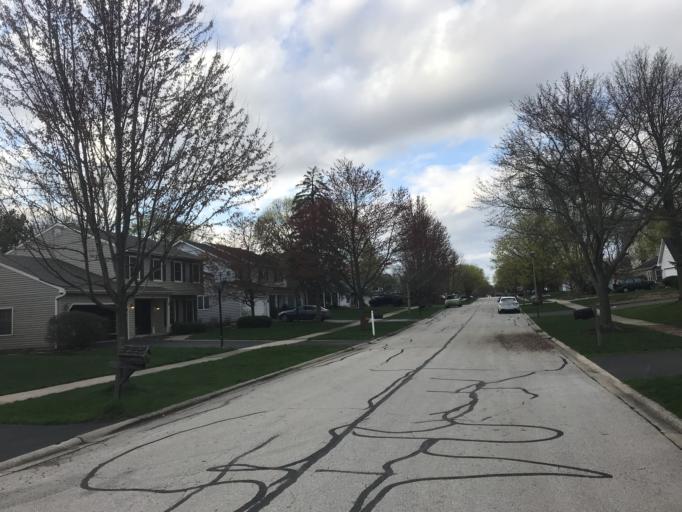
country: US
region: Illinois
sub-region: Will County
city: Bolingbrook
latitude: 41.7300
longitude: -88.1126
